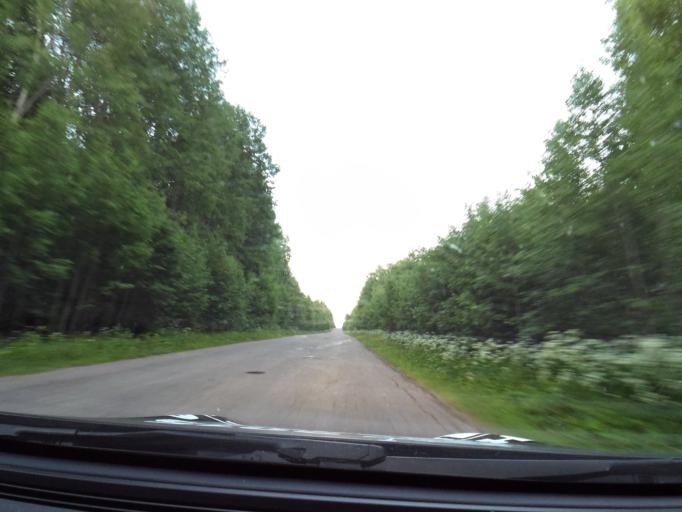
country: RU
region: Leningrad
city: Voznesen'ye
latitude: 60.8443
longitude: 35.6165
